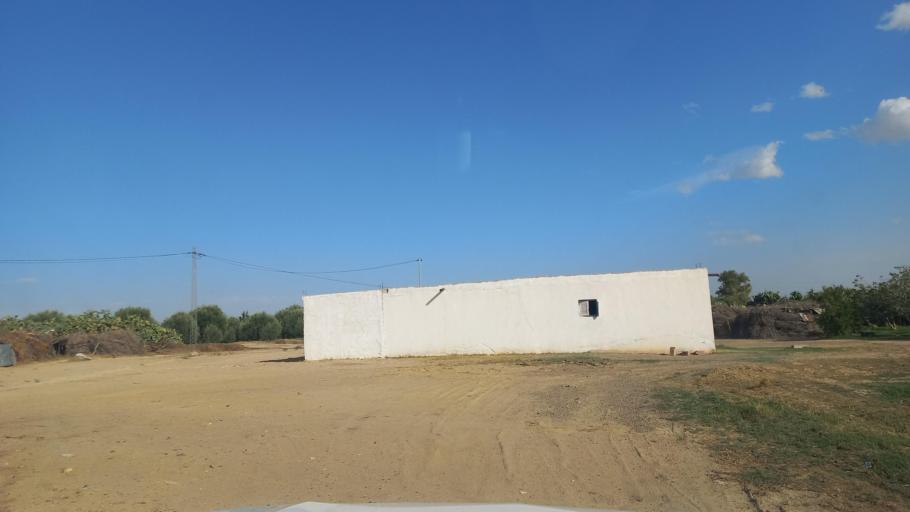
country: TN
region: Al Qasrayn
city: Kasserine
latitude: 35.2564
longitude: 9.0306
